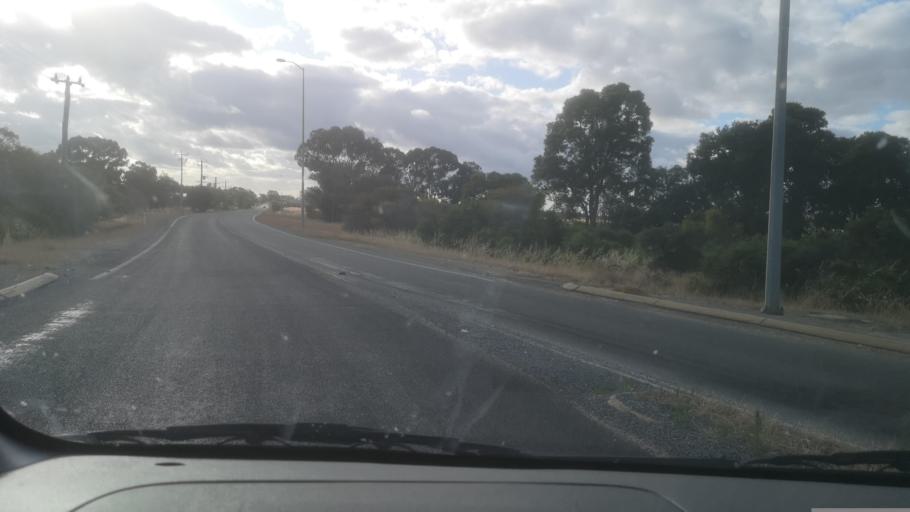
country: AU
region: Western Australia
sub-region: Wanneroo
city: Yanchep
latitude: -31.3326
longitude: 115.8679
